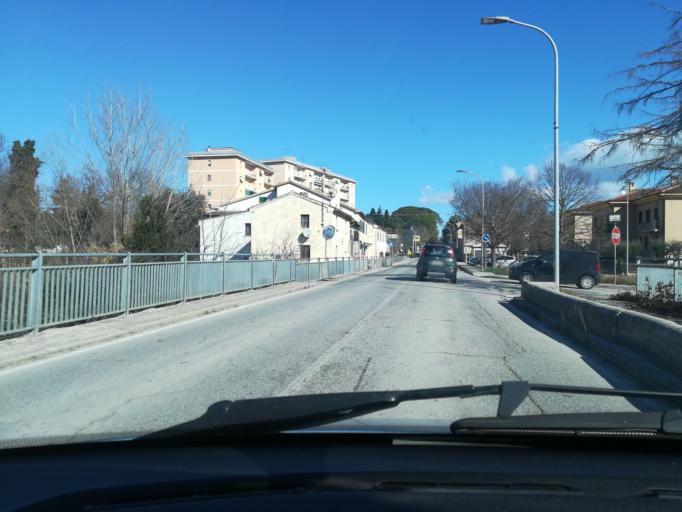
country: IT
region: The Marches
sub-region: Provincia di Macerata
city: Montecassiano
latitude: 43.3457
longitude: 13.4335
